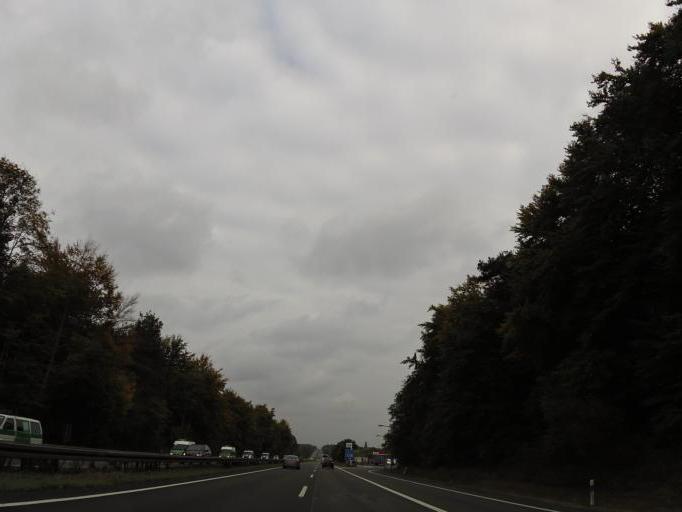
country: DE
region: Saarland
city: Homburg
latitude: 49.3452
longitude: 7.3075
